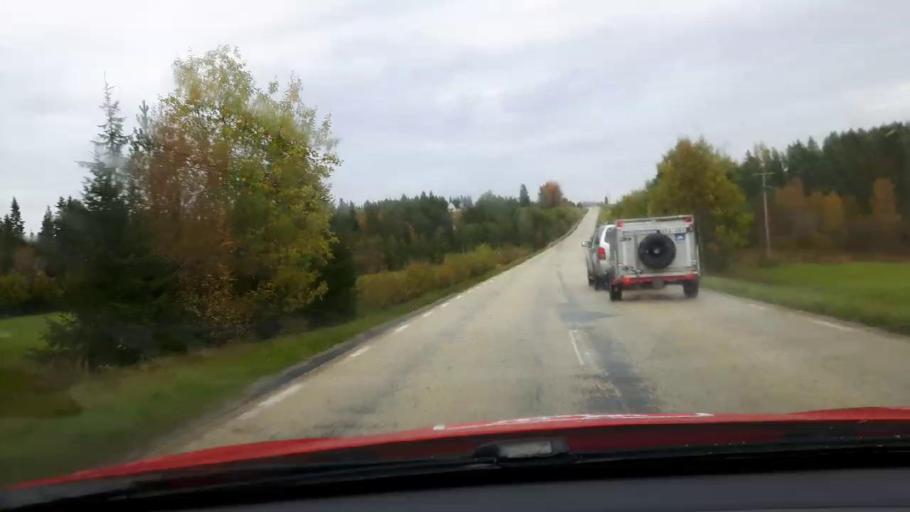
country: SE
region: Jaemtland
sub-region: Bergs Kommun
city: Hoverberg
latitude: 62.9541
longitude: 14.3401
